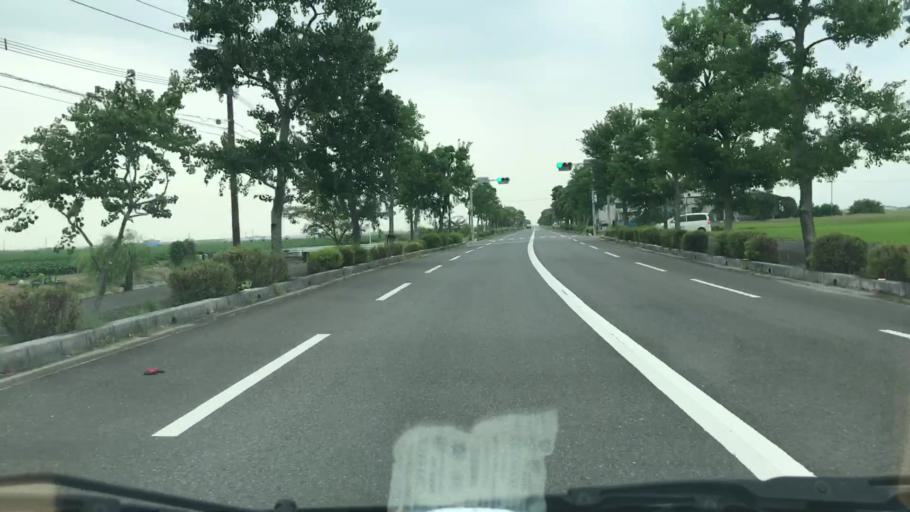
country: JP
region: Saga Prefecture
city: Okawa
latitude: 33.1922
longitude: 130.3034
